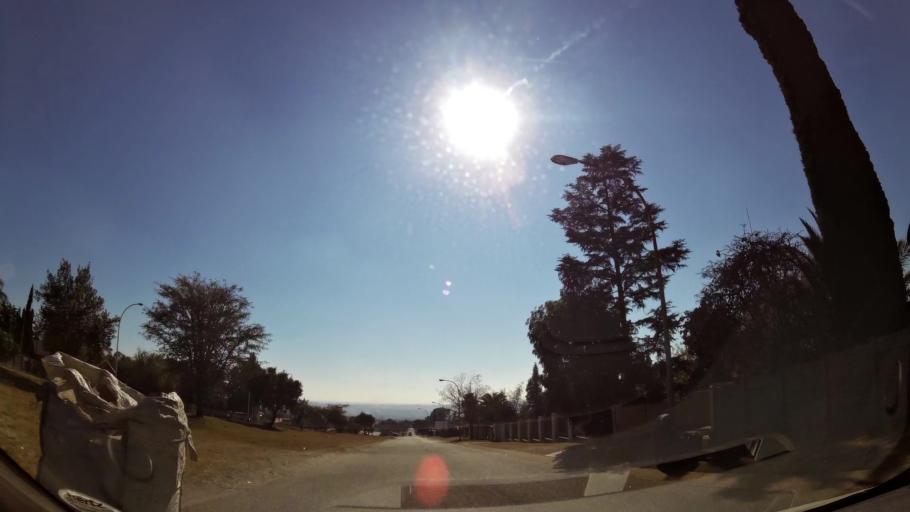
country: ZA
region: Mpumalanga
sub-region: Nkangala District Municipality
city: Witbank
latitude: -25.8692
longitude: 29.2409
